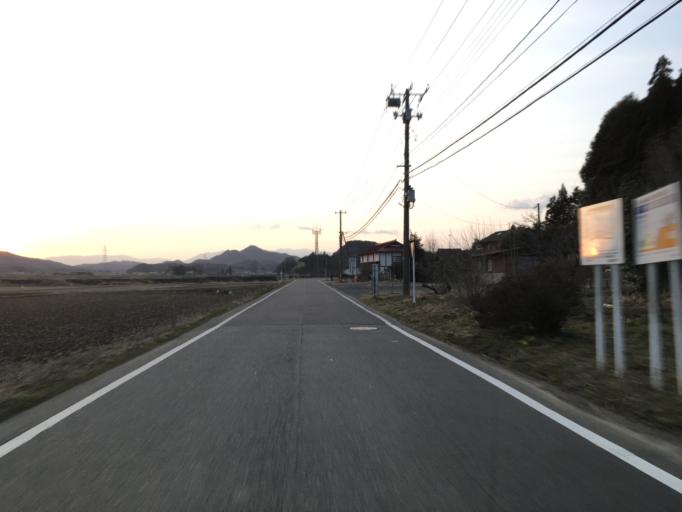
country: JP
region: Fukushima
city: Ishikawa
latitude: 37.0680
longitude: 140.3119
